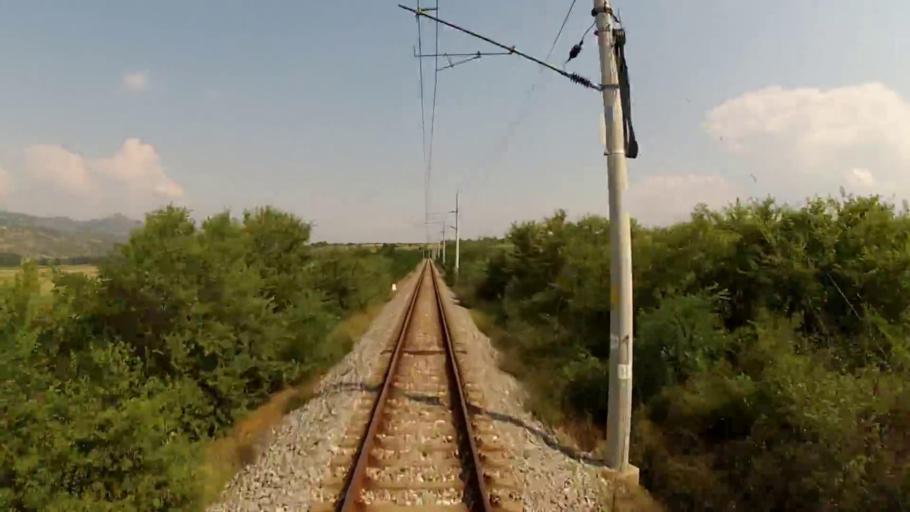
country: BG
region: Blagoevgrad
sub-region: Obshtina Sandanski
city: Sandanski
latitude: 41.5602
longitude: 23.2424
